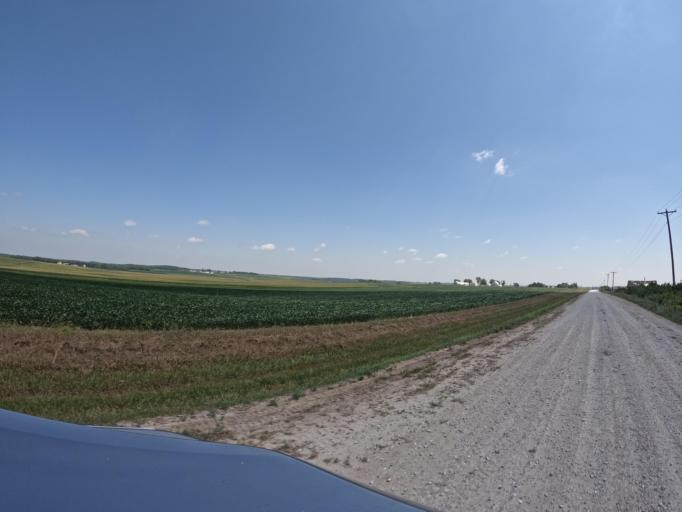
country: US
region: Iowa
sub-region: Keokuk County
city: Sigourney
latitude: 41.2794
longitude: -92.2266
